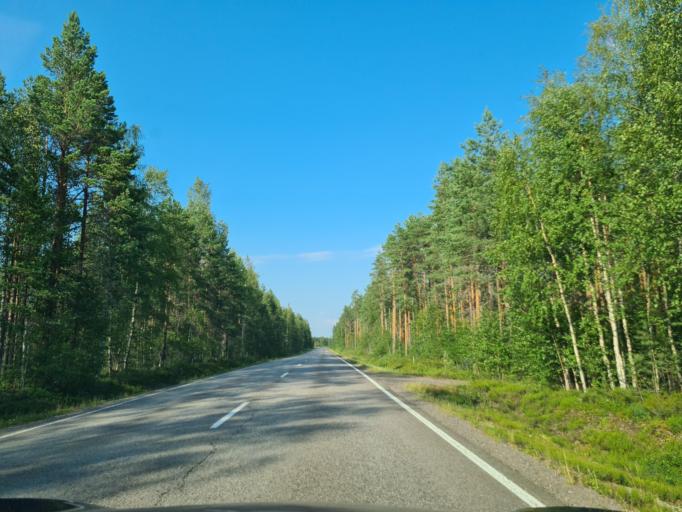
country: FI
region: Satakunta
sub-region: Pohjois-Satakunta
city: Karvia
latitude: 62.3082
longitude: 22.6480
